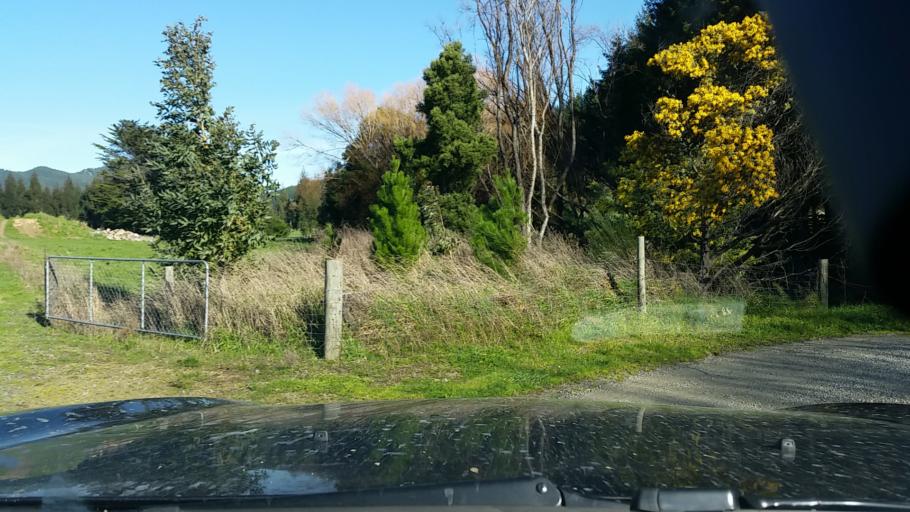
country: NZ
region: Marlborough
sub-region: Marlborough District
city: Blenheim
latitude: -41.4043
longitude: 173.7718
